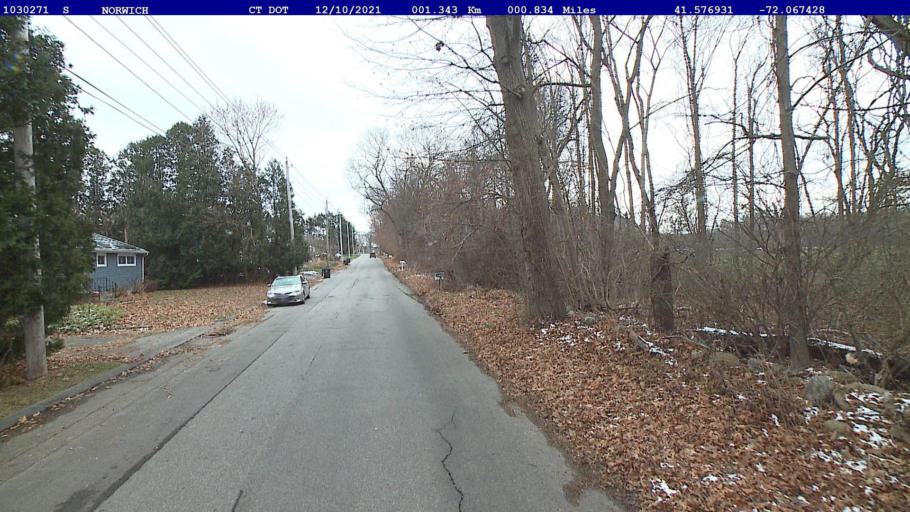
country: US
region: Connecticut
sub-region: New London County
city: Baltic
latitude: 41.5769
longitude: -72.0674
